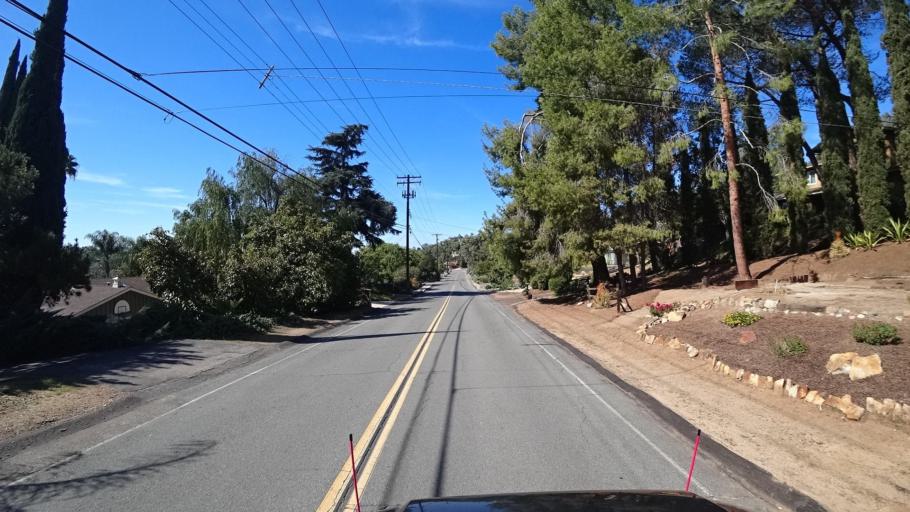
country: US
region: California
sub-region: San Diego County
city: Casa de Oro-Mount Helix
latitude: 32.7578
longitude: -116.9592
